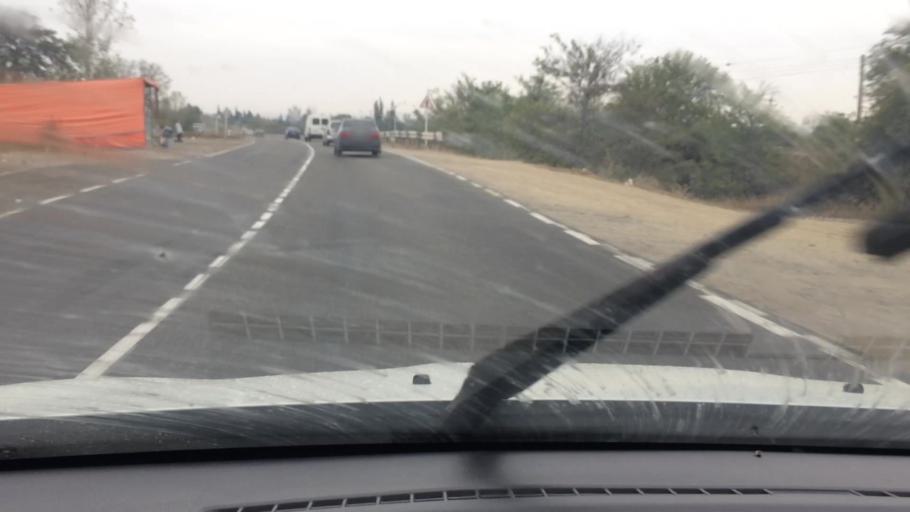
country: GE
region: Kvemo Kartli
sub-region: Marneuli
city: Marneuli
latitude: 41.4035
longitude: 44.8303
